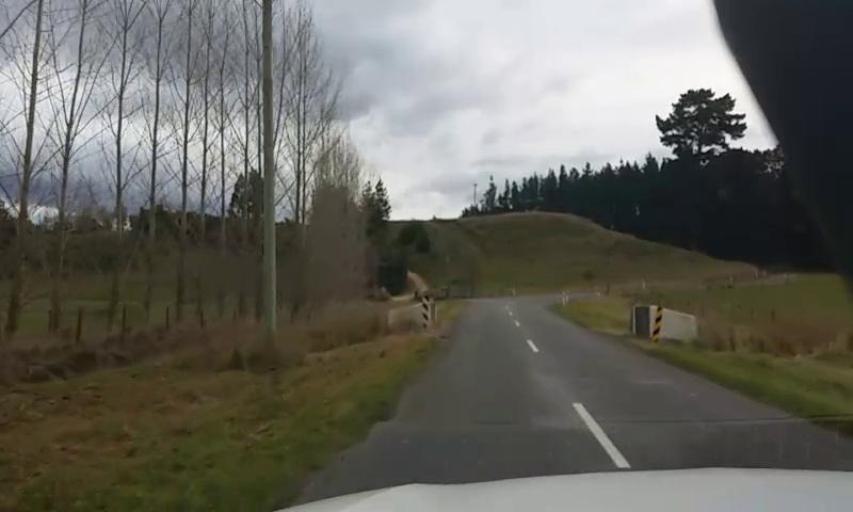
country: NZ
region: Canterbury
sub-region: Waimakariri District
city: Kaiapoi
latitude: -43.2993
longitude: 172.4378
